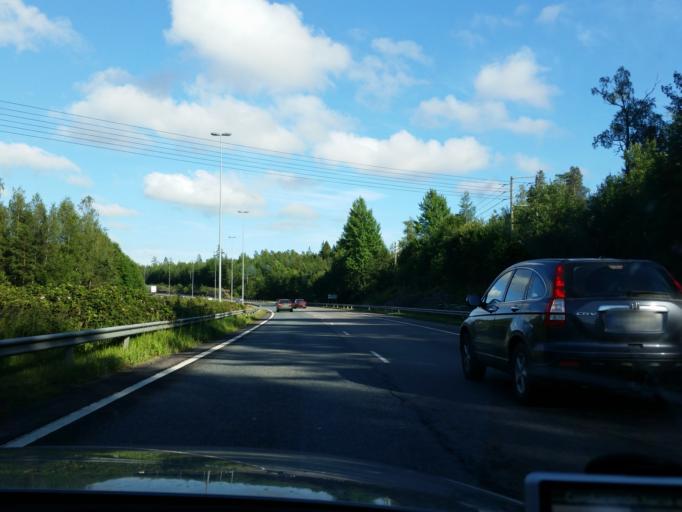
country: FI
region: Uusimaa
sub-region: Helsinki
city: Kirkkonummi
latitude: 60.2570
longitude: 24.5021
